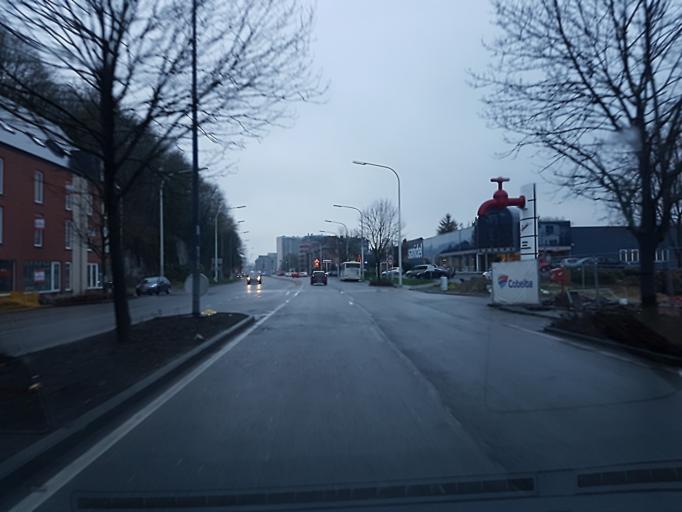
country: BE
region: Wallonia
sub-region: Province de Namur
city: Namur
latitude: 50.4643
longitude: 4.8958
